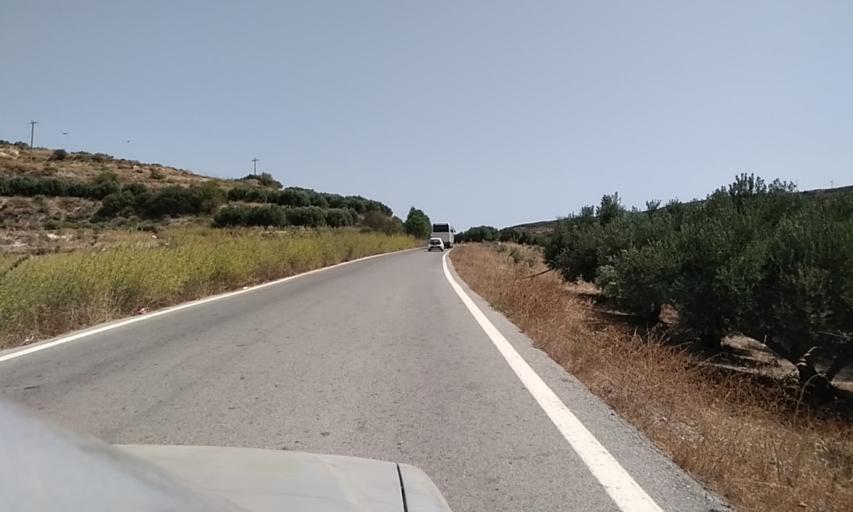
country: GR
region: Crete
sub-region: Nomos Lasithiou
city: Makry-Gialos
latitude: 35.0986
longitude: 26.0621
